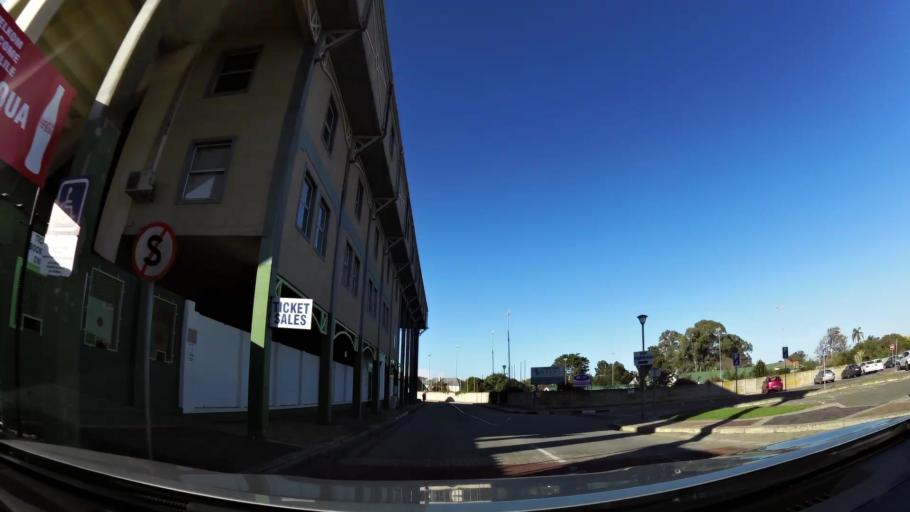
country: ZA
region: Western Cape
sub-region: Eden District Municipality
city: George
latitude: -33.9529
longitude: 22.4470
